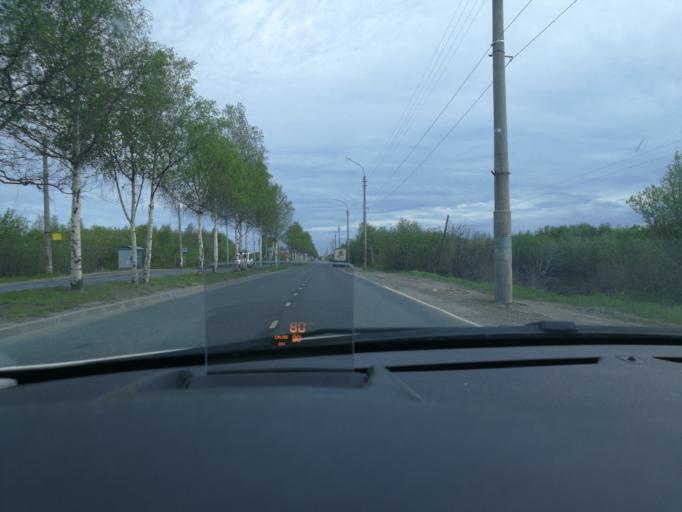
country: RU
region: Arkhangelskaya
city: Arkhangel'sk
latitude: 64.6144
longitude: 40.5254
